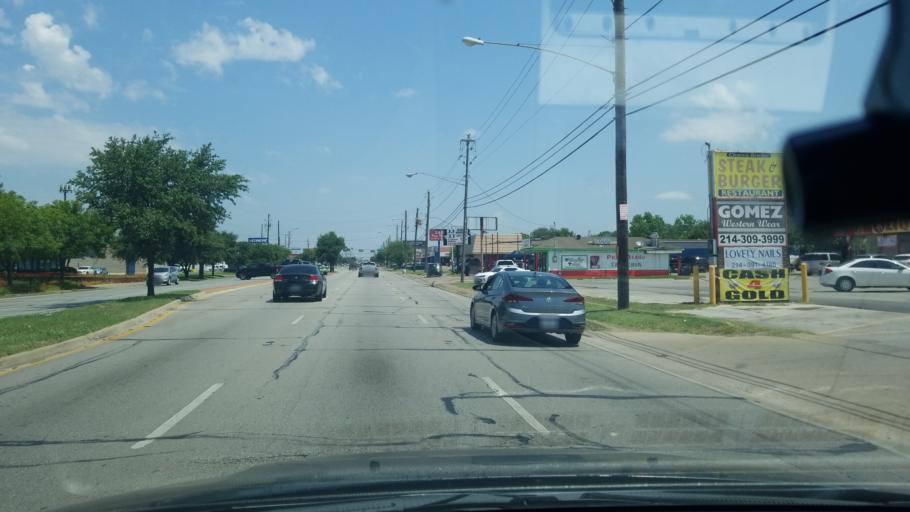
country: US
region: Texas
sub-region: Dallas County
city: Balch Springs
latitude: 32.7397
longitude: -96.6828
